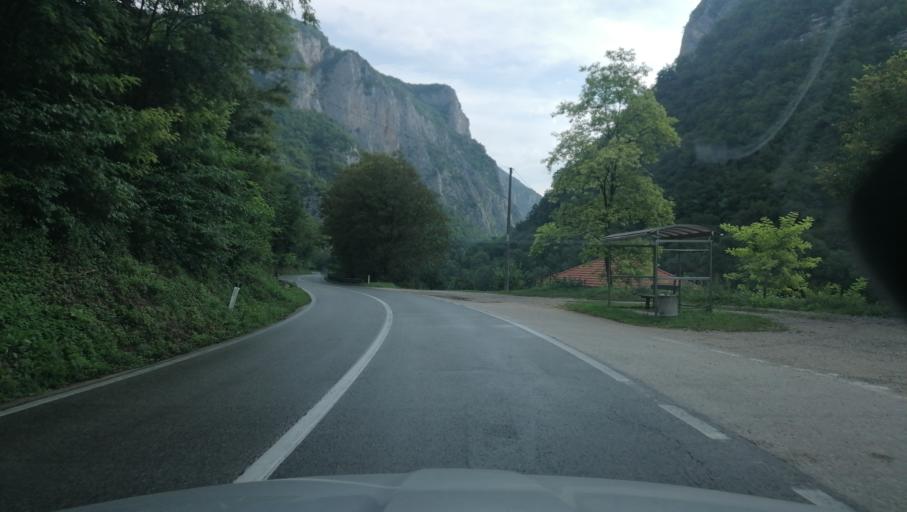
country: BA
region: Republika Srpska
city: Hiseti
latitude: 44.6774
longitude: 17.1661
